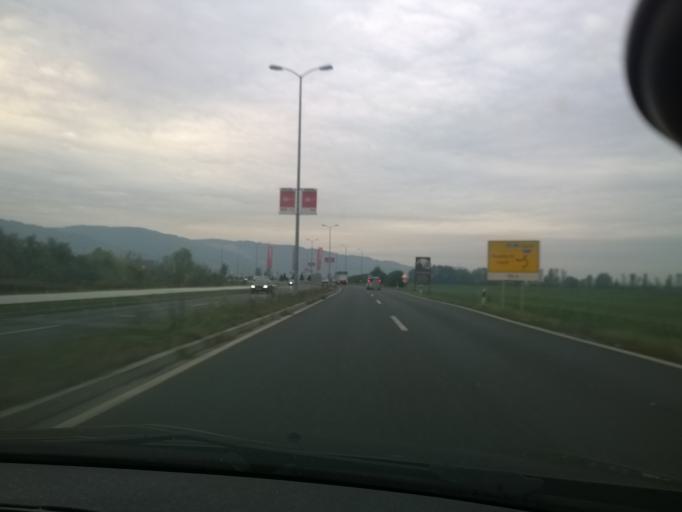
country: HR
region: Zagrebacka
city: Zapresic
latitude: 45.8735
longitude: 15.8204
